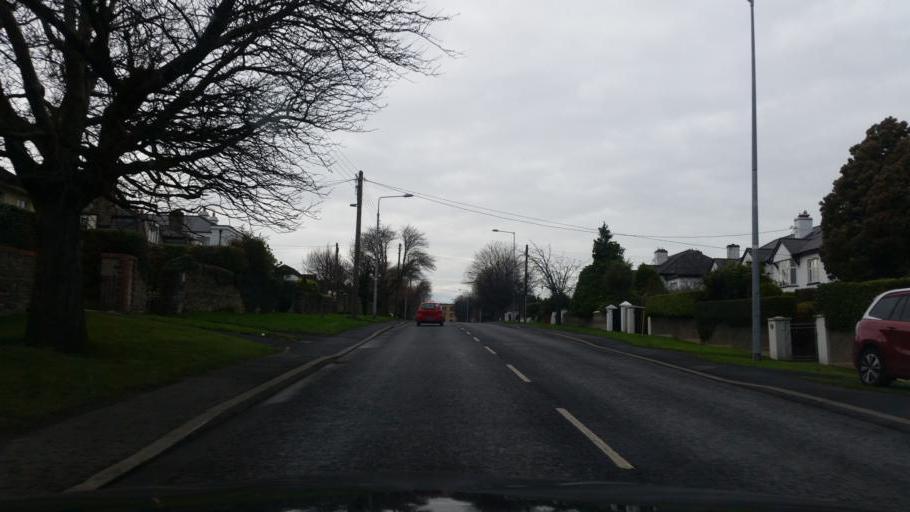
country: IE
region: Leinster
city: Mount Merrion
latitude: 53.3009
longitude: -6.2155
